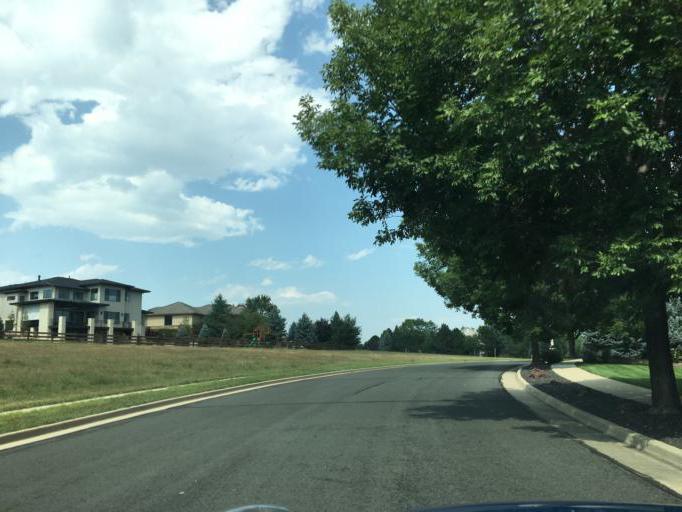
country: US
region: Colorado
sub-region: Boulder County
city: Lafayette
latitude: 40.0172
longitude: -105.1201
